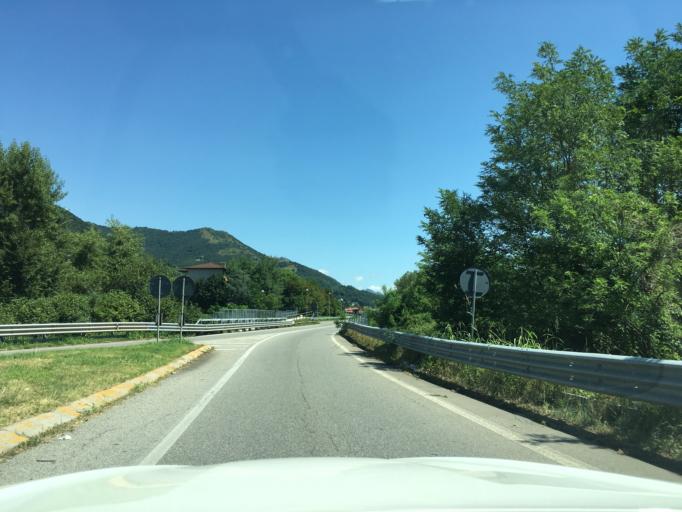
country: IT
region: Lombardy
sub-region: Provincia di Bergamo
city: Villa di Serio
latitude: 45.7357
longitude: 9.7445
